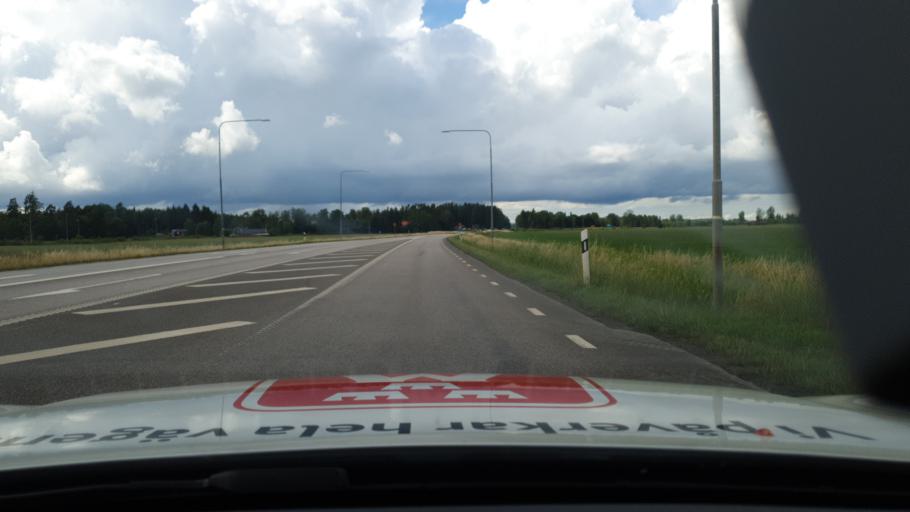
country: SE
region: Vaestra Goetaland
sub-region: Tidaholms Kommun
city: Olofstorp
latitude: 58.3542
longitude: 14.0499
